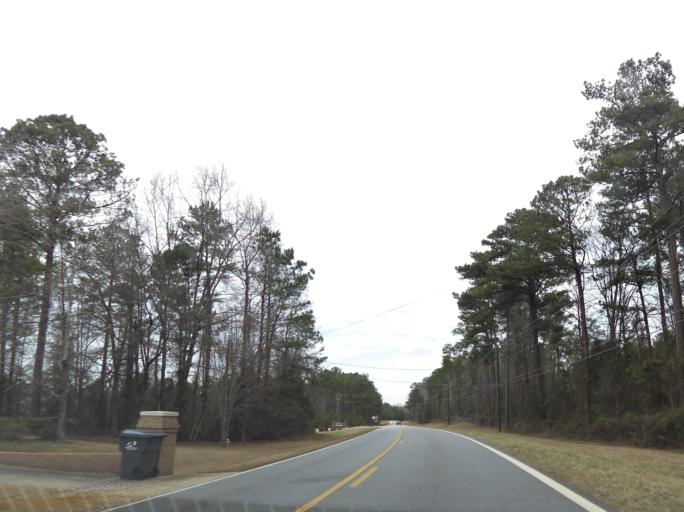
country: US
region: Georgia
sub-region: Bibb County
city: West Point
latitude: 32.8565
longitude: -83.7840
